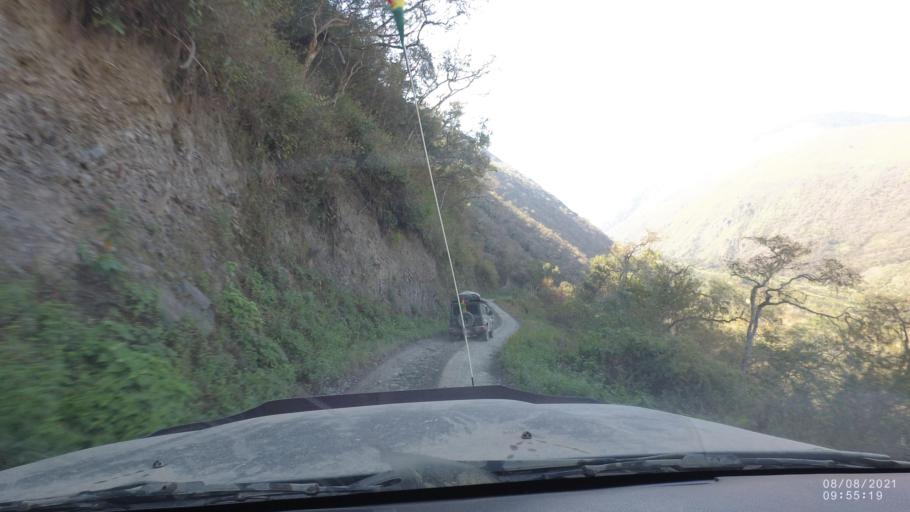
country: BO
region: La Paz
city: Quime
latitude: -16.6340
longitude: -66.7302
